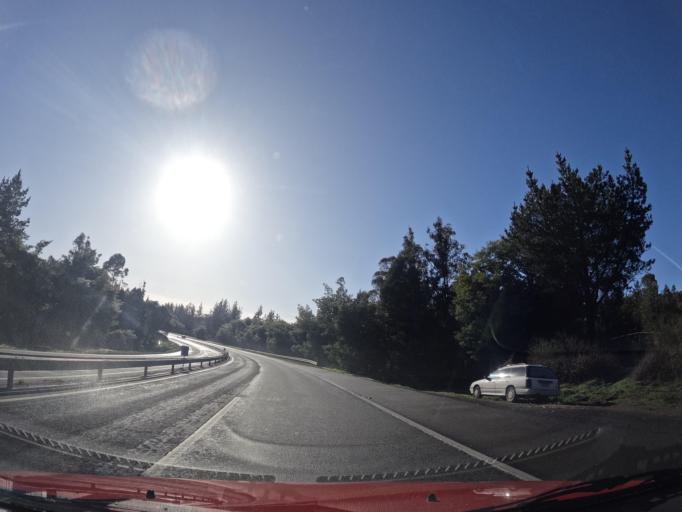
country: CL
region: Biobio
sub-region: Provincia de Concepcion
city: Penco
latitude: -36.7593
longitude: -72.9293
